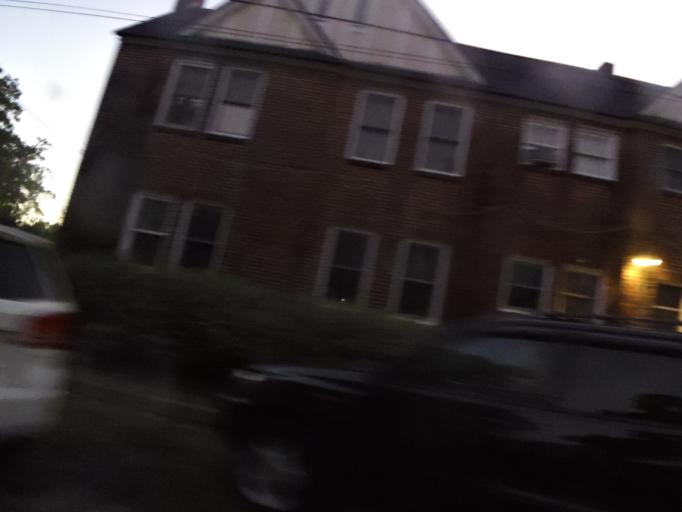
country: US
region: Florida
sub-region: Duval County
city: Jacksonville
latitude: 30.2973
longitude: -81.7050
